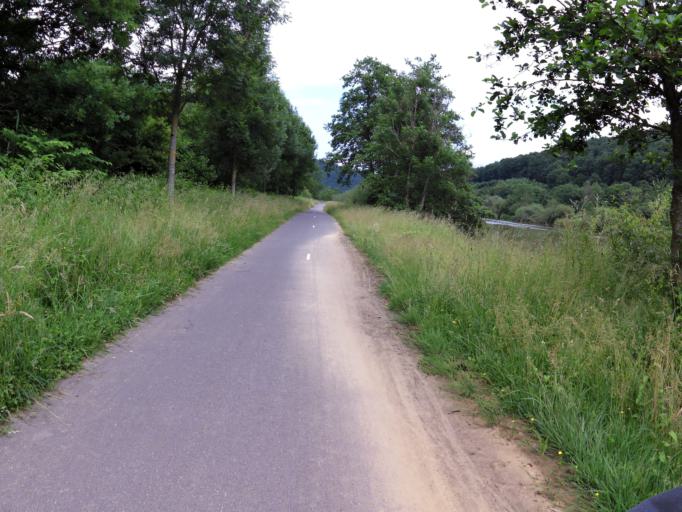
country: FR
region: Champagne-Ardenne
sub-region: Departement des Ardennes
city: Nouzonville
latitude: 49.8276
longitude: 4.7466
